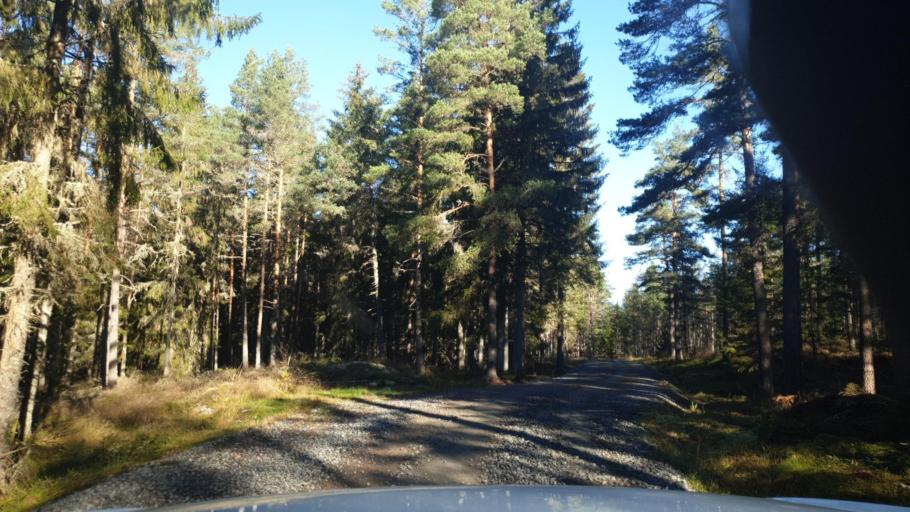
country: SE
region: Vaermland
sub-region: Karlstads Kommun
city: Valberg
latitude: 59.4551
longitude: 13.0963
